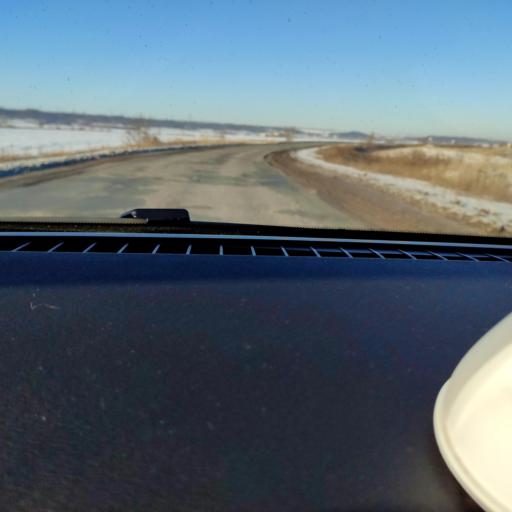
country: RU
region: Samara
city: Spiridonovka
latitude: 53.1262
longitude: 50.6201
